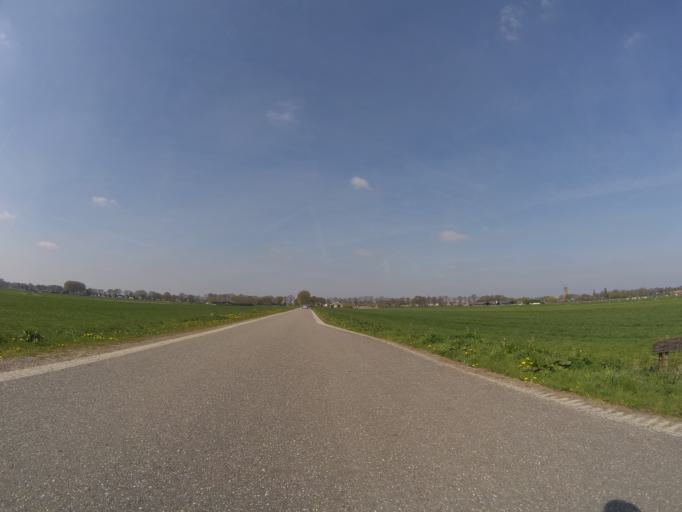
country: NL
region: Utrecht
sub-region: Gemeente Baarn
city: Baarn
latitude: 52.2455
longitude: 5.2740
